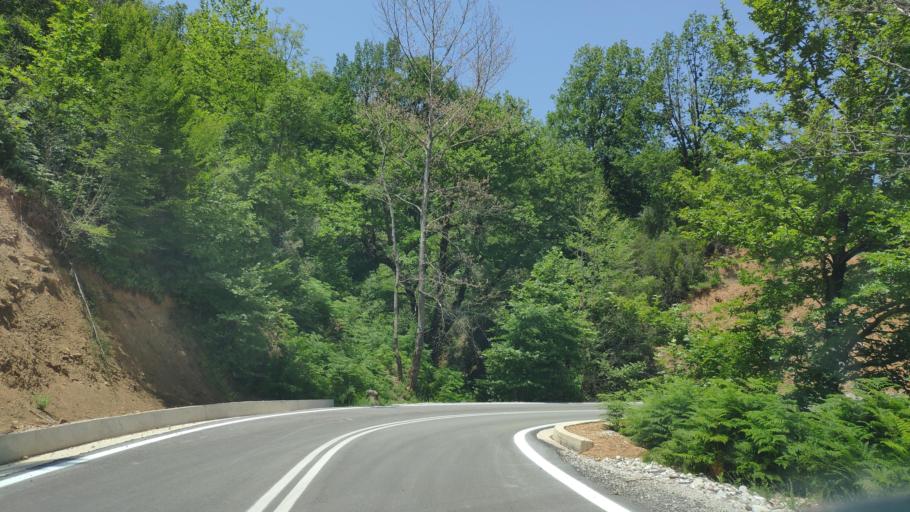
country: GR
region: Epirus
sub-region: Nomos Artas
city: Ano Kalentini
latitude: 39.1781
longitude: 21.3573
